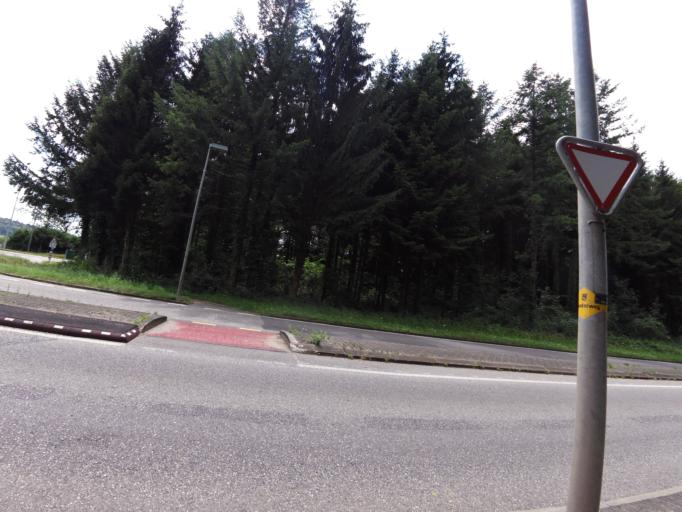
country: CH
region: Bern
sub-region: Oberaargau
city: Aarwangen
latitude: 47.2475
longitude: 7.7550
